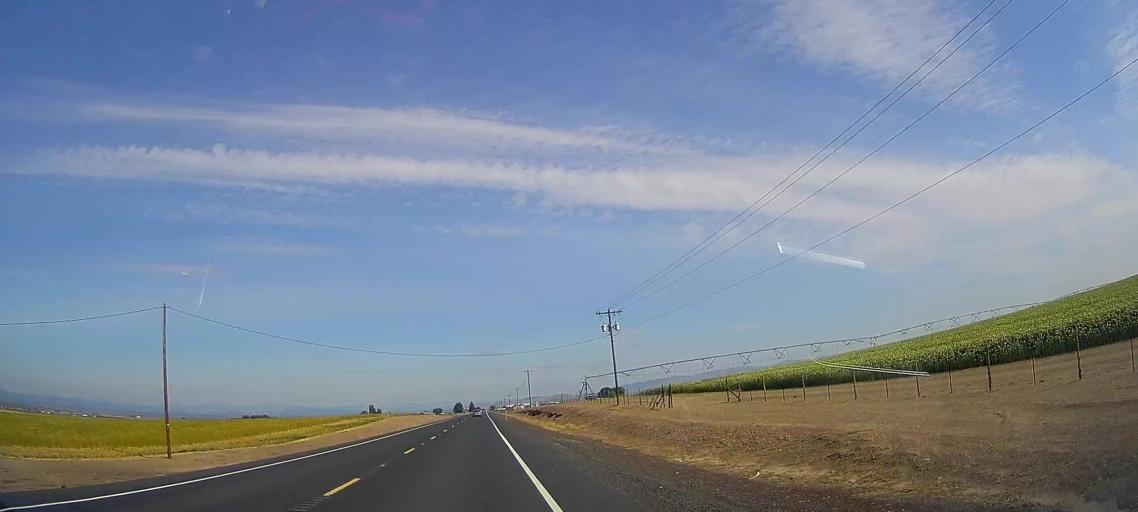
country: US
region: Oregon
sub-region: Jefferson County
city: Madras
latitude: 44.6837
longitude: -121.1496
